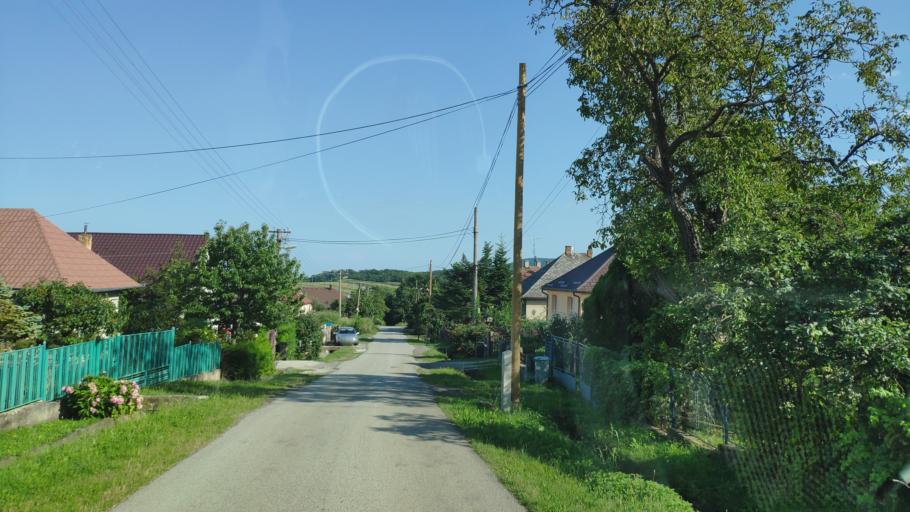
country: SK
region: Kosicky
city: Secovce
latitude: 48.6321
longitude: 21.4832
